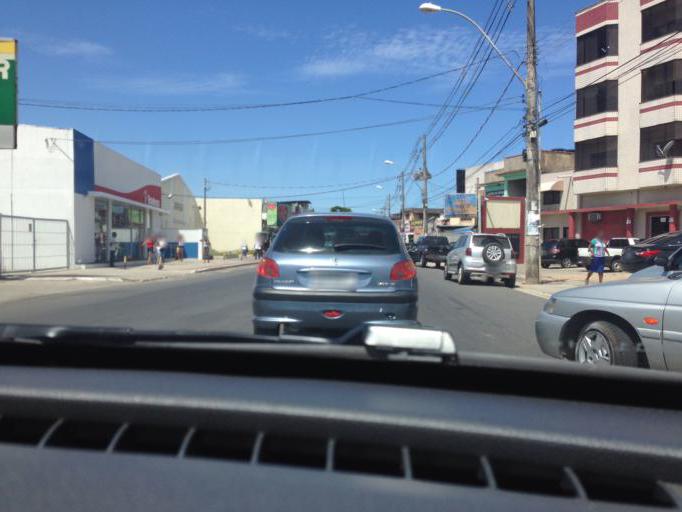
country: BR
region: Espirito Santo
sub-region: Guarapari
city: Guarapari
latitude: -20.6532
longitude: -40.4965
